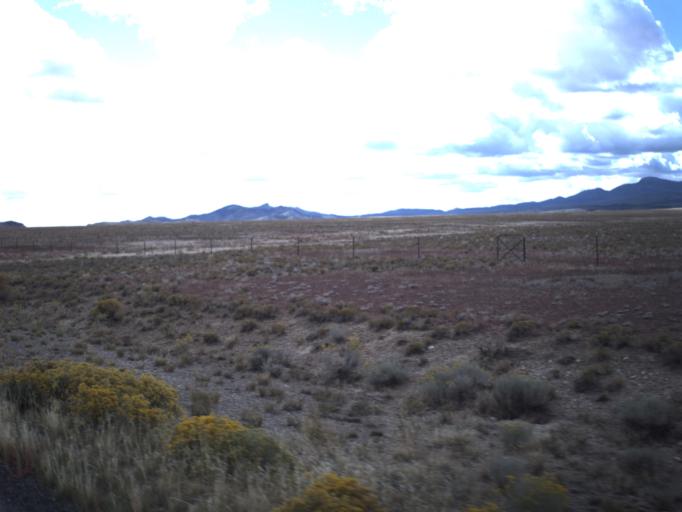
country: US
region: Utah
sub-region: Beaver County
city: Milford
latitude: 38.6462
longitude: -113.8658
